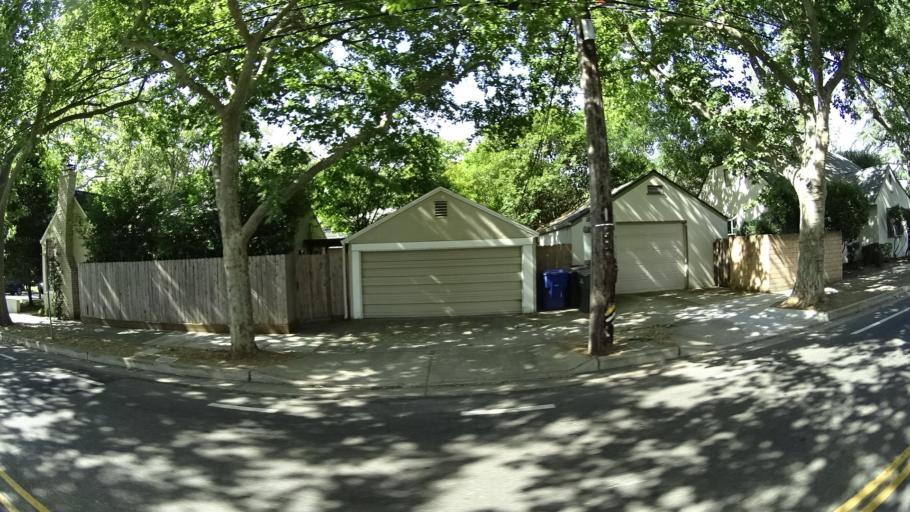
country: US
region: California
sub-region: Sacramento County
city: Sacramento
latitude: 38.5712
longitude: -121.4502
